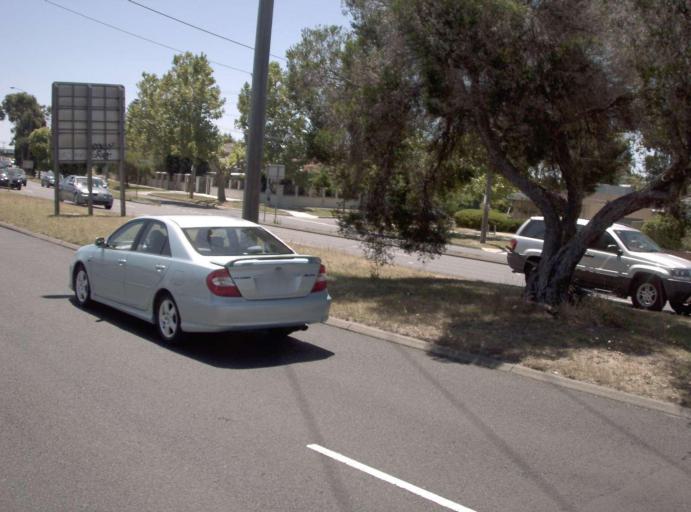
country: AU
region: Victoria
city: Hughesdale
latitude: -37.8924
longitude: 145.0850
